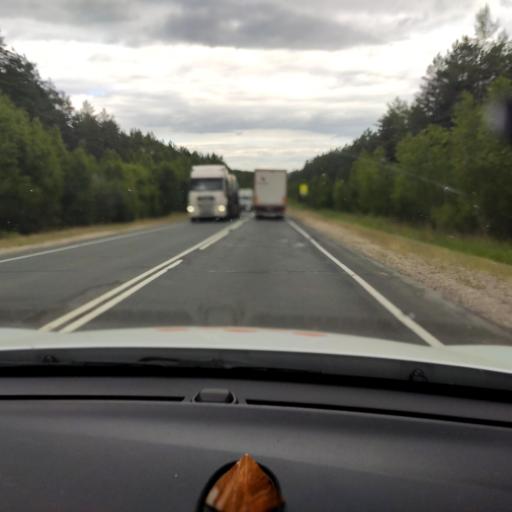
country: RU
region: Mariy-El
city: Volzhsk
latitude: 55.9056
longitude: 48.3781
